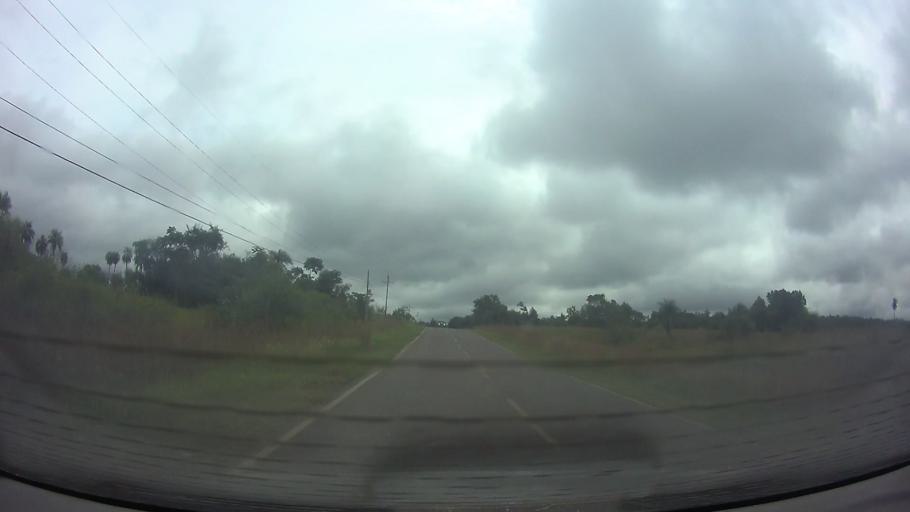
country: PY
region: Cordillera
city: Atyra
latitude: -25.2844
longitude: -57.1933
